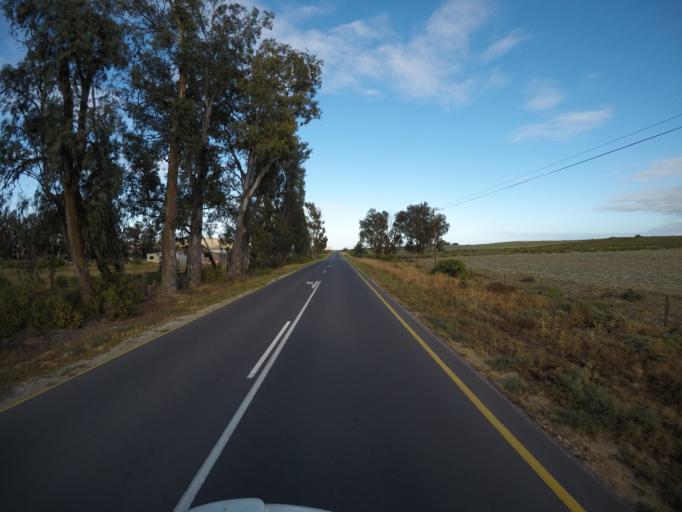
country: ZA
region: Western Cape
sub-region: West Coast District Municipality
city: Clanwilliam
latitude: -32.3116
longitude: 18.3792
